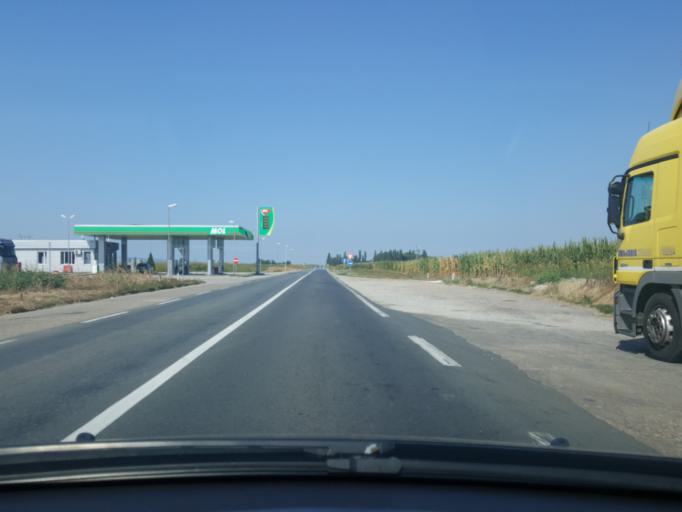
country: RS
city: Jarak
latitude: 44.9326
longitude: 19.7831
